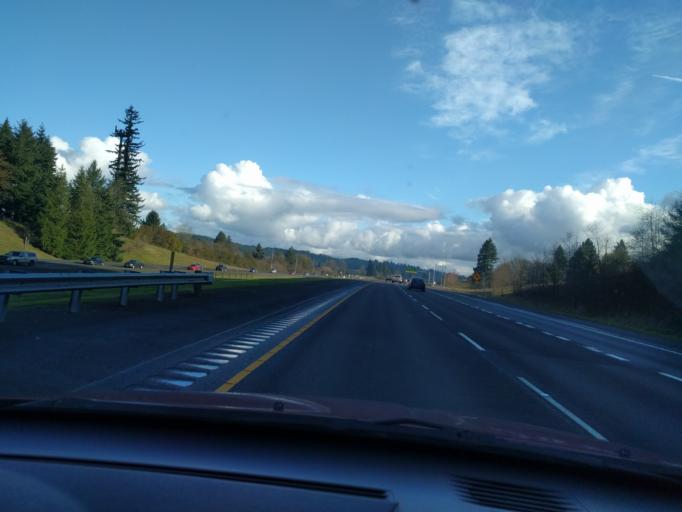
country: US
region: Oregon
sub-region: Clackamas County
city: Stafford
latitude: 45.3723
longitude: -122.7160
